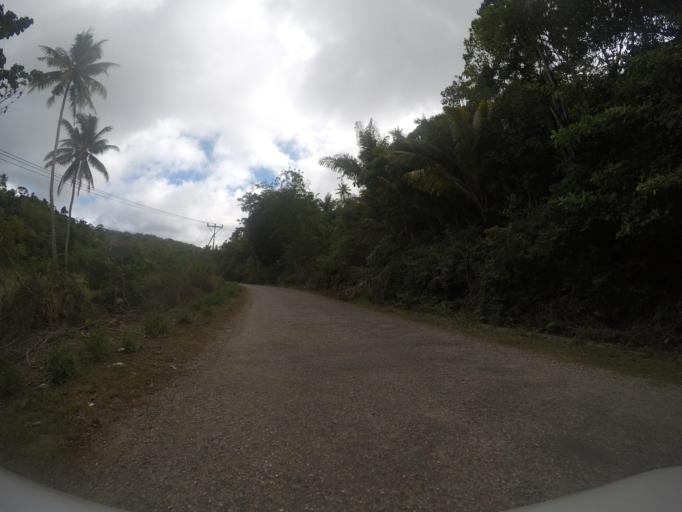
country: TL
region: Lautem
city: Lospalos
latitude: -8.5398
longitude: 126.9546
